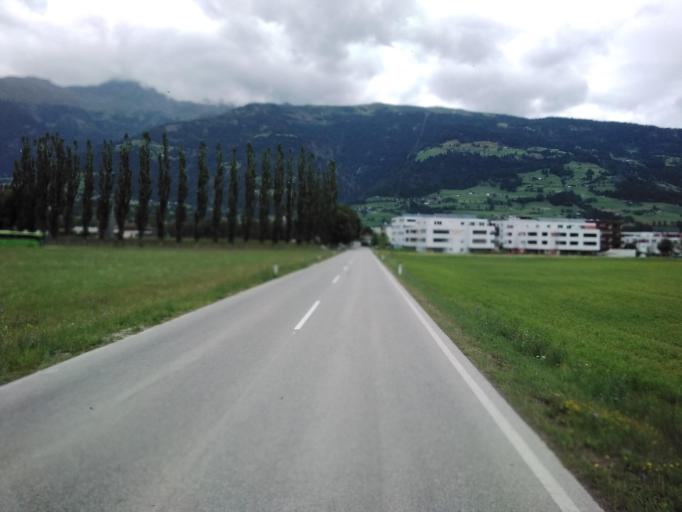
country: AT
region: Tyrol
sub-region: Politischer Bezirk Lienz
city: Amlach
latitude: 46.8215
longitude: 12.7675
